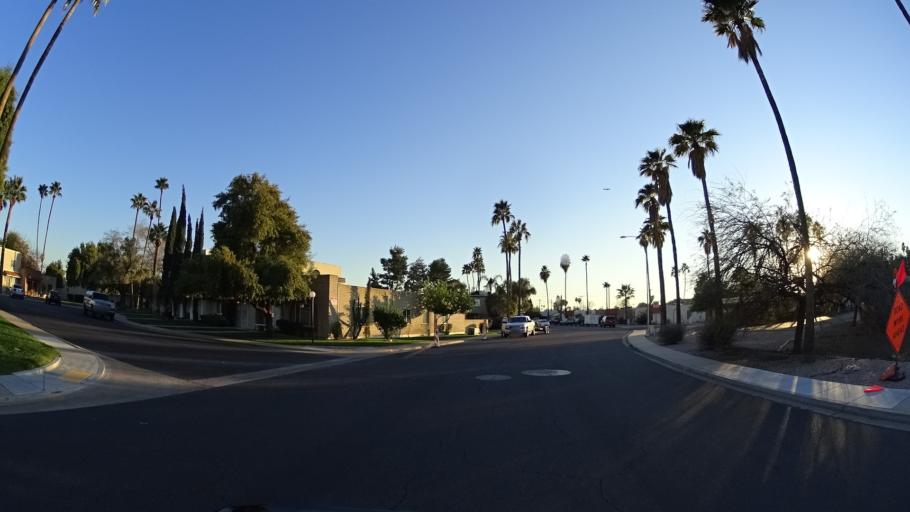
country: US
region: Arizona
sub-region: Maricopa County
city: Mesa
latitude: 33.4245
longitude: -111.8202
